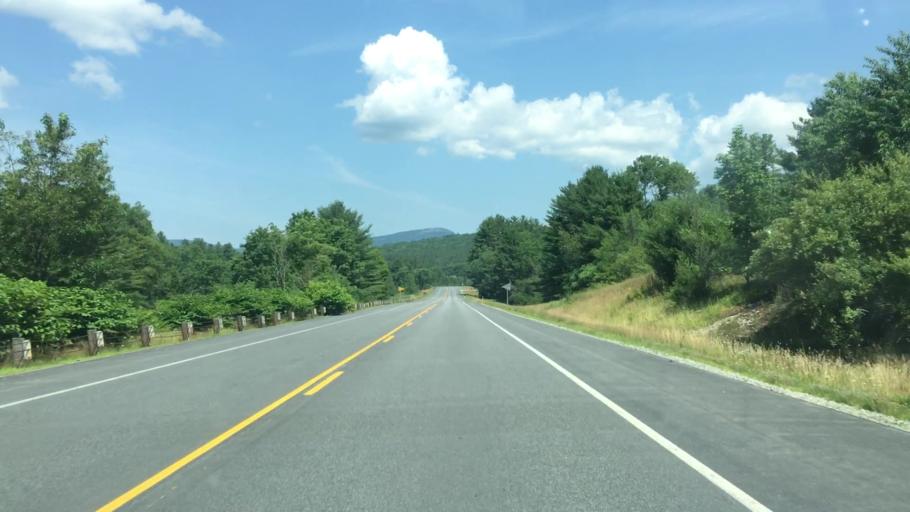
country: US
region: New Hampshire
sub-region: Sullivan County
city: Newport
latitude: 43.4060
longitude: -72.1854
